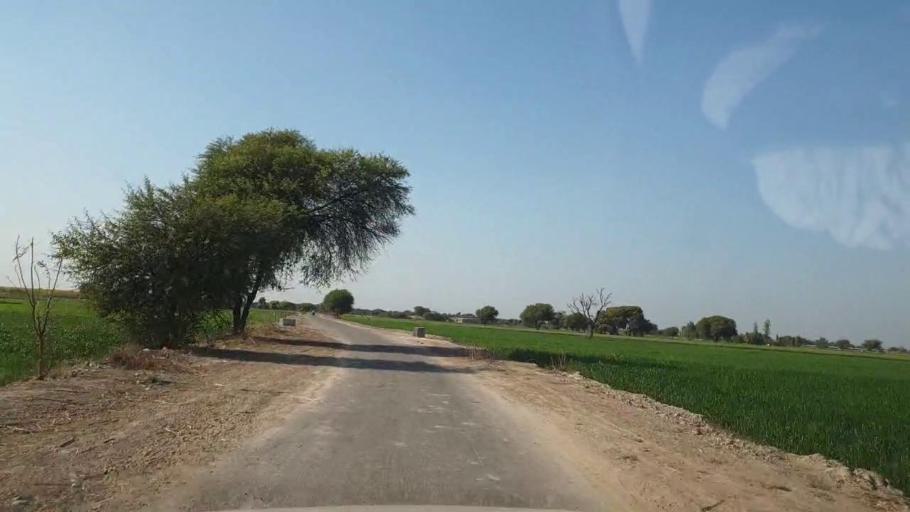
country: PK
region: Sindh
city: Tando Allahyar
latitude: 25.4839
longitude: 68.6599
